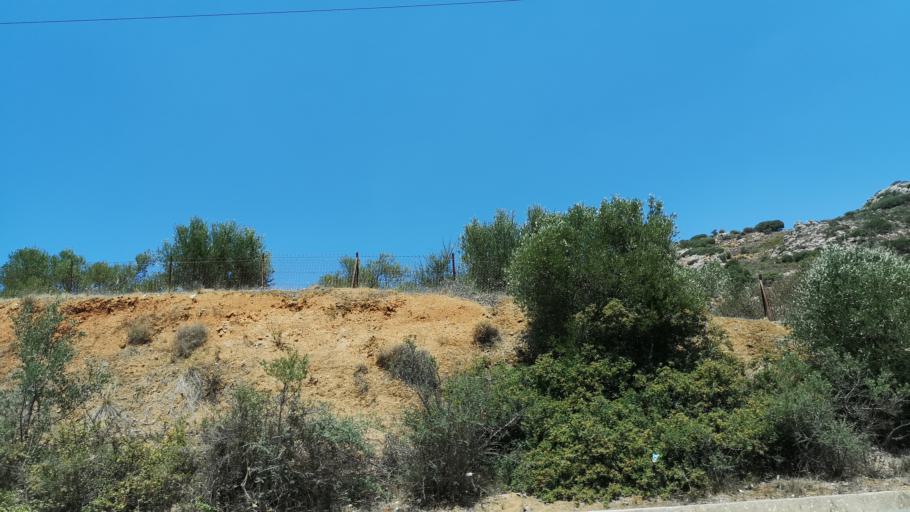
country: GR
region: Crete
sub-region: Nomos Lasithiou
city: Neapoli
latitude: 35.2293
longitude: 25.6552
